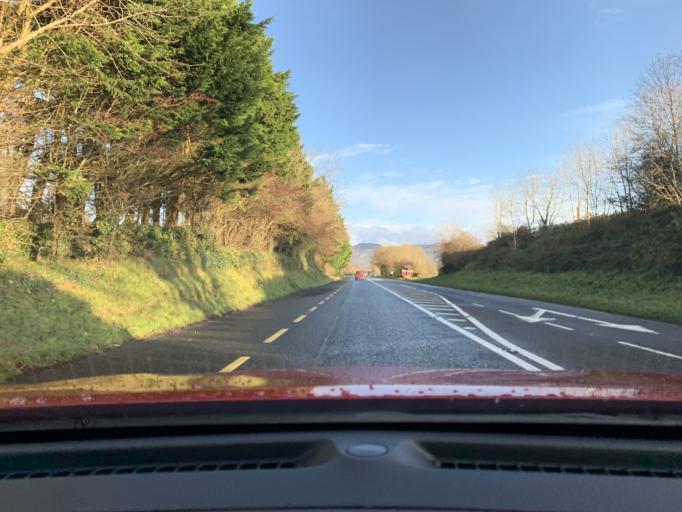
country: IE
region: Connaught
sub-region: Sligo
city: Sligo
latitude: 54.2953
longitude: -8.4730
